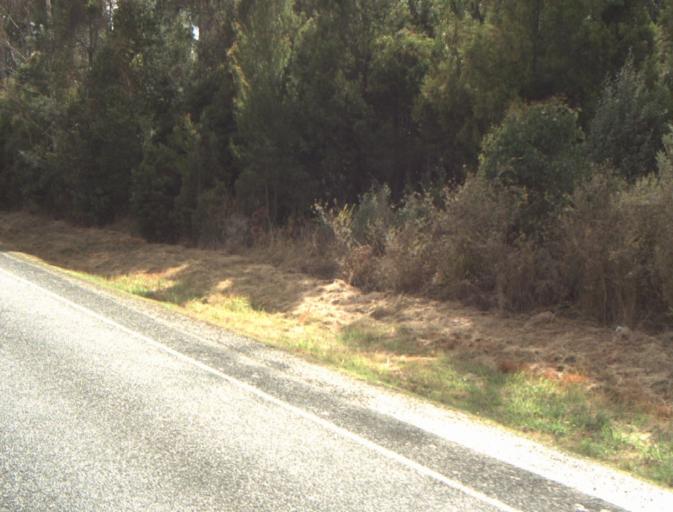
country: AU
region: Tasmania
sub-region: Launceston
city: Mayfield
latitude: -41.2658
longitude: 147.2150
